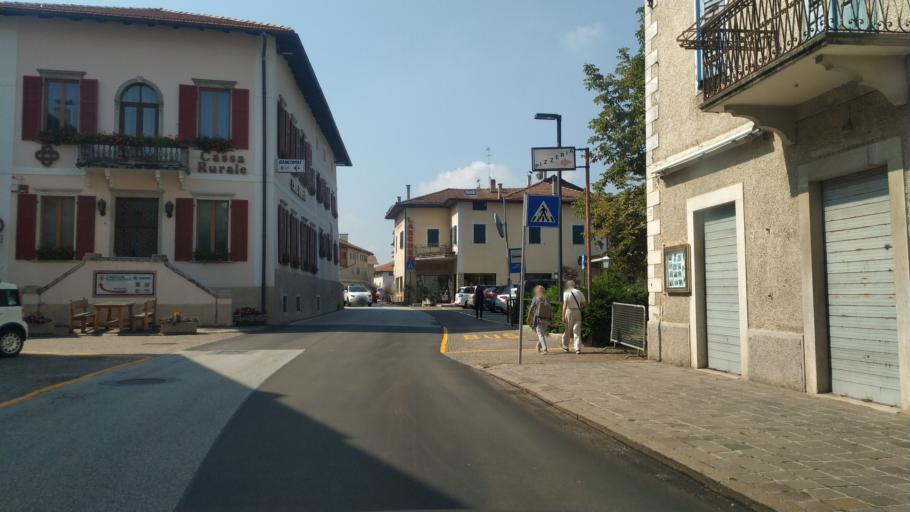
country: IT
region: Trentino-Alto Adige
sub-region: Provincia di Trento
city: Cavareno
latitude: 46.4096
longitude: 11.1376
